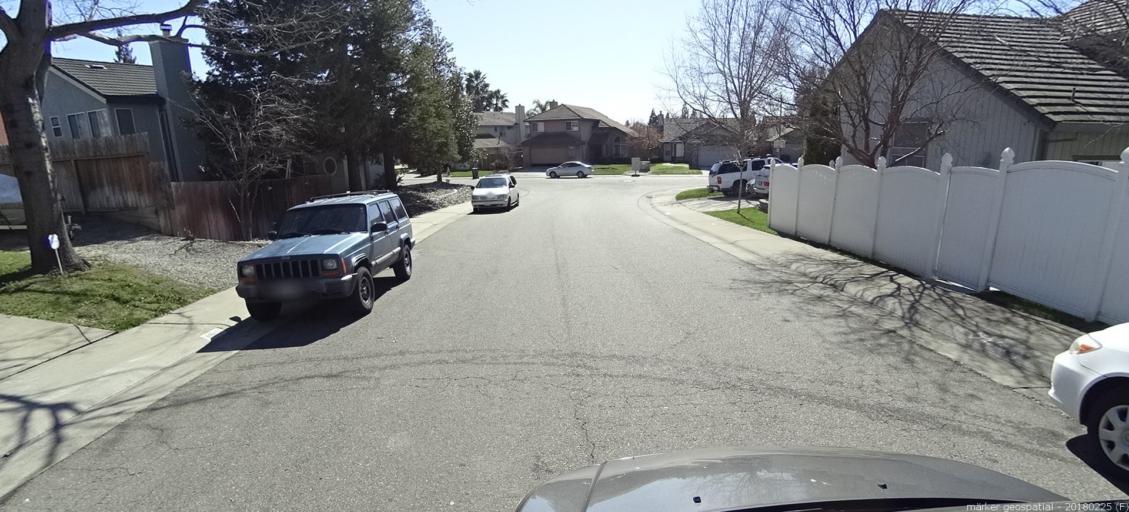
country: US
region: California
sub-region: Sacramento County
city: Antelope
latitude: 38.7214
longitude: -121.3545
